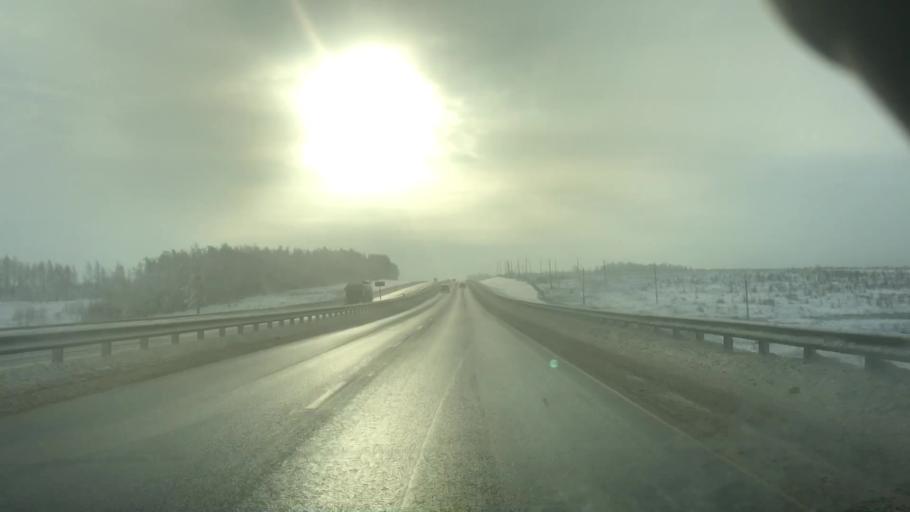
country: RU
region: Tula
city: Venev
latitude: 54.3195
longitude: 38.1544
